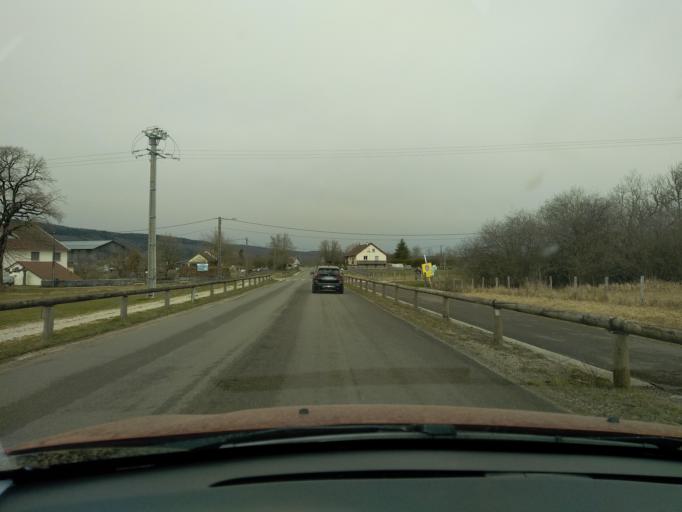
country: FR
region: Franche-Comte
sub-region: Departement du Jura
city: Champagnole
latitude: 46.7093
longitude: 5.7865
